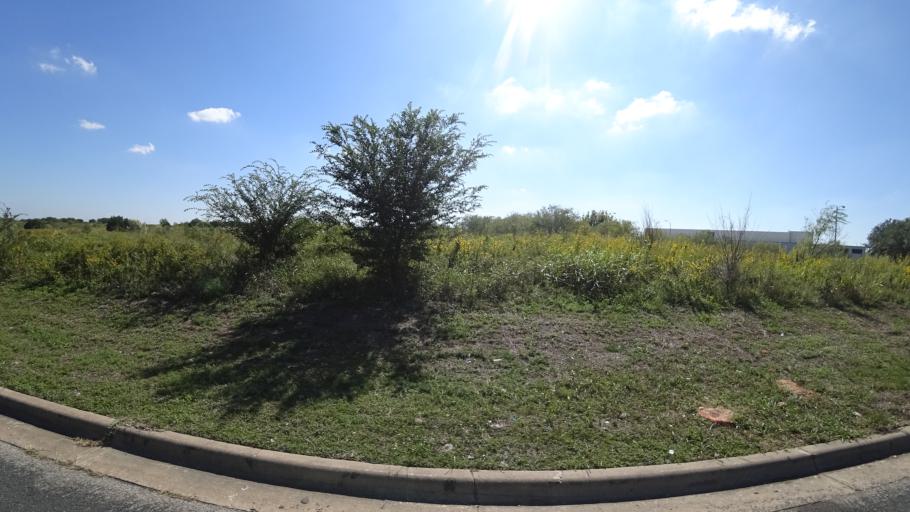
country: US
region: Texas
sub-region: Travis County
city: Manor
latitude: 30.3423
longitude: -97.6126
